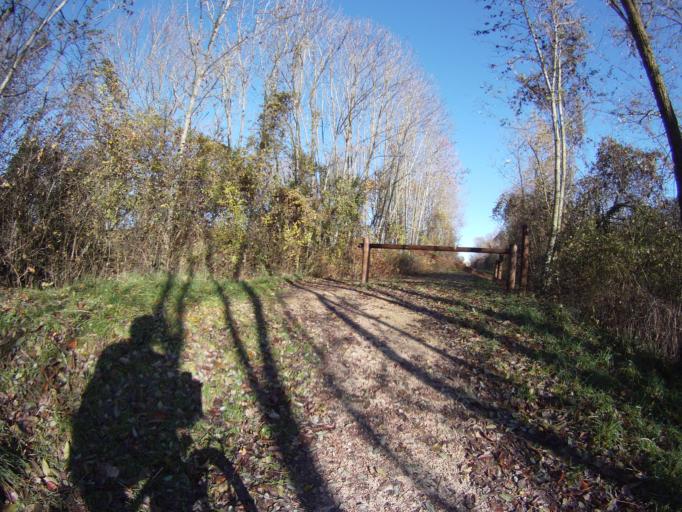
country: FR
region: Lorraine
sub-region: Departement de Meurthe-et-Moselle
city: Faulx
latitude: 48.7921
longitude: 6.2296
